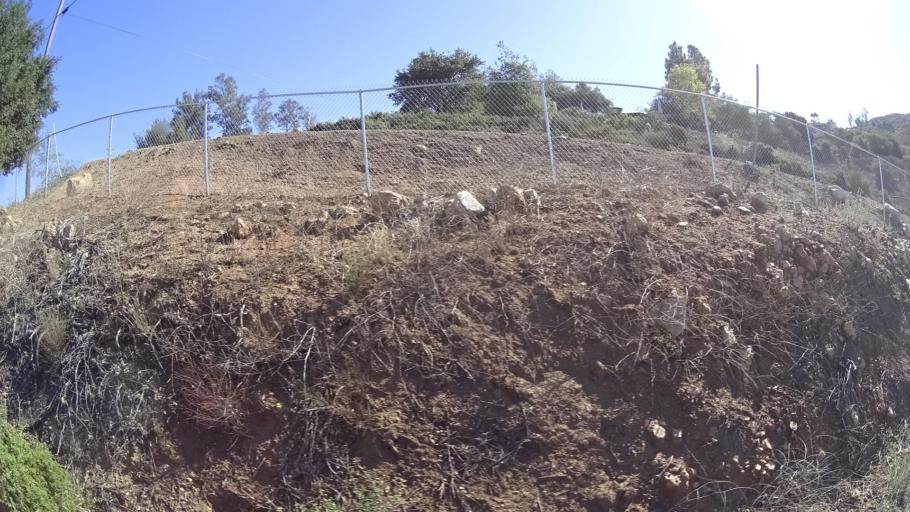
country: US
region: California
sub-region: San Diego County
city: Jamul
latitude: 32.7286
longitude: -116.8325
